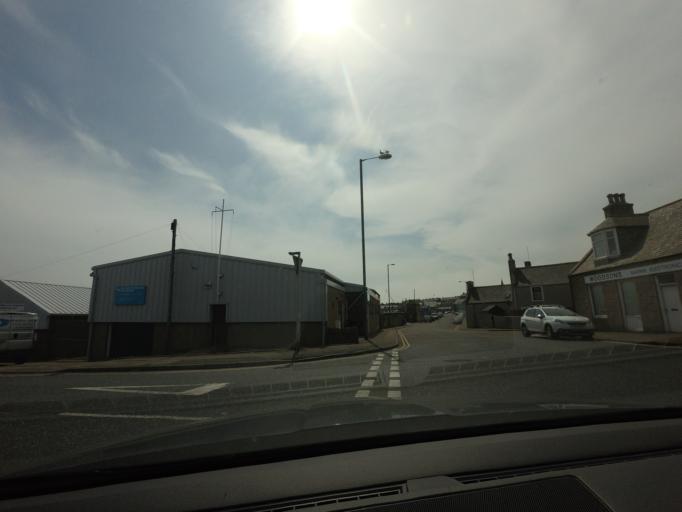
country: GB
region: Scotland
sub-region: Aberdeenshire
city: Peterhead
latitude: 57.5089
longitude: -1.7751
